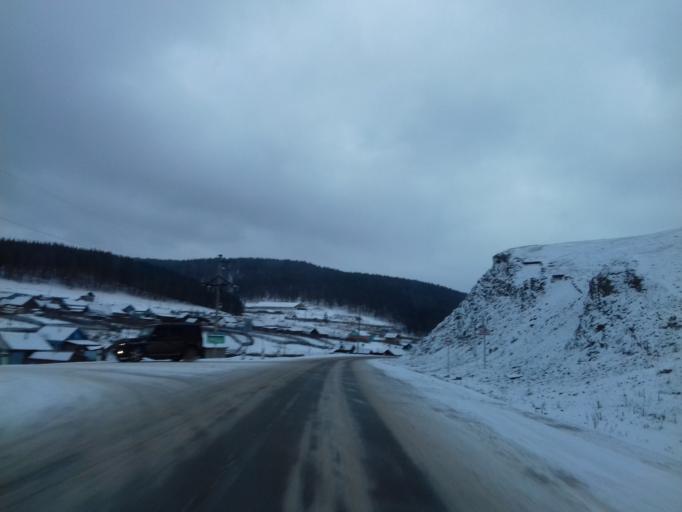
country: RU
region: Bashkortostan
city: Verkhniy Avzyan
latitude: 53.3288
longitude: 57.6287
